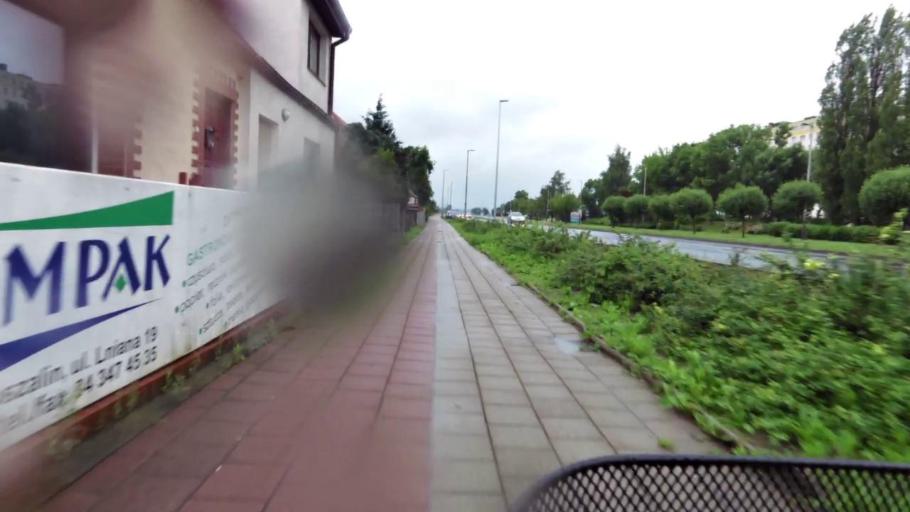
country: PL
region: West Pomeranian Voivodeship
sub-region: Koszalin
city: Koszalin
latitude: 54.2084
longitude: 16.1827
